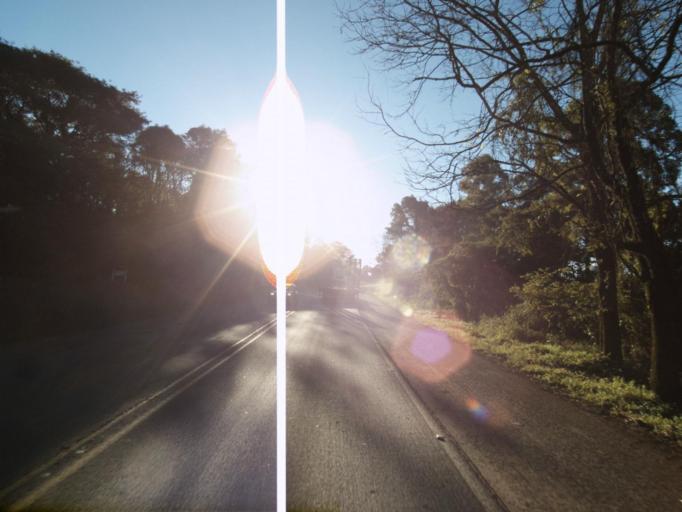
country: BR
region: Santa Catarina
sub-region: Chapeco
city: Chapeco
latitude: -26.8912
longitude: -52.9317
